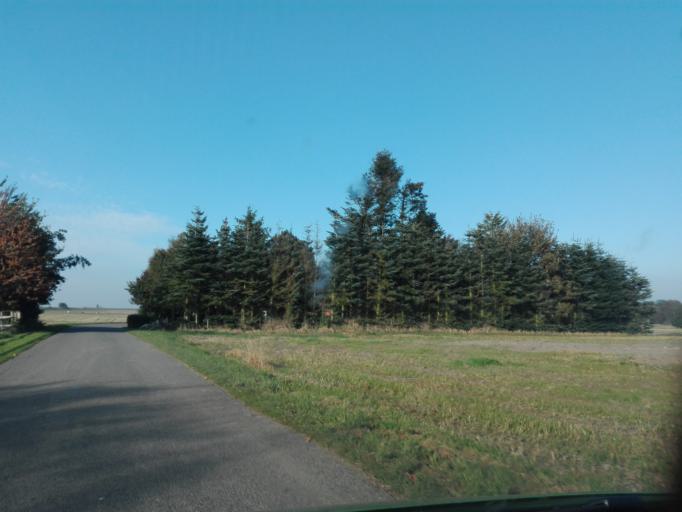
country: DK
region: Central Jutland
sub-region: Odder Kommune
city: Odder
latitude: 55.9259
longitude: 10.1873
